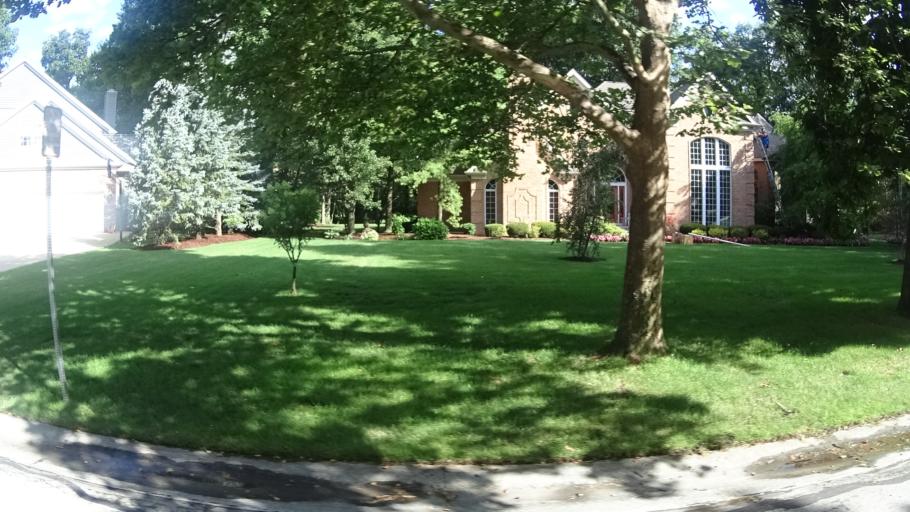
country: US
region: Ohio
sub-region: Erie County
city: Sandusky
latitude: 41.4169
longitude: -82.6581
